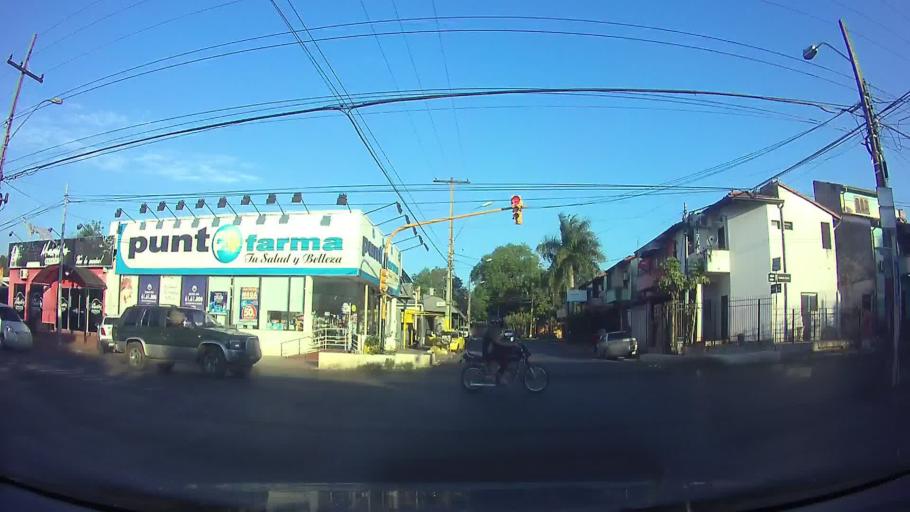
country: PY
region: Central
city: Lambare
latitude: -25.3350
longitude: -57.5681
